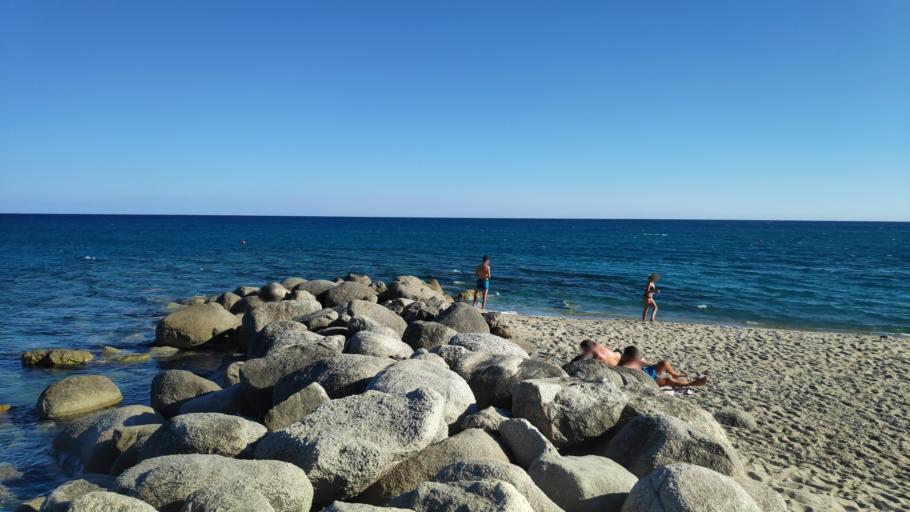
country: IT
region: Calabria
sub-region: Provincia di Reggio Calabria
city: Roccella Ionica
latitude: 38.3180
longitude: 16.3981
